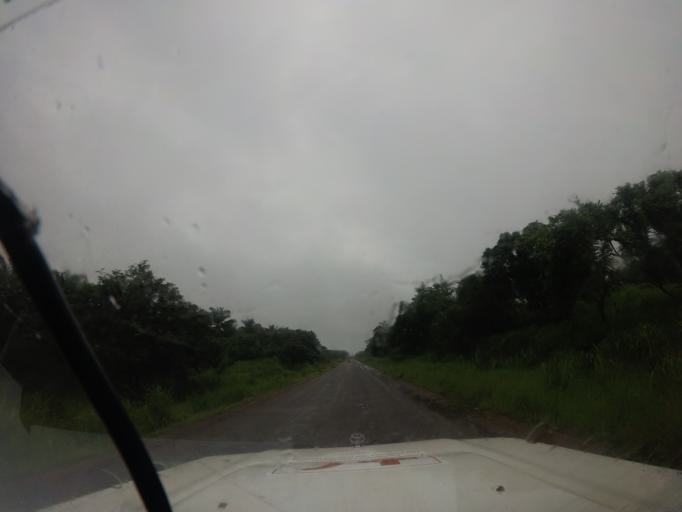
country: SL
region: Northern Province
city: Binkolo
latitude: 8.9455
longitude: -11.9871
